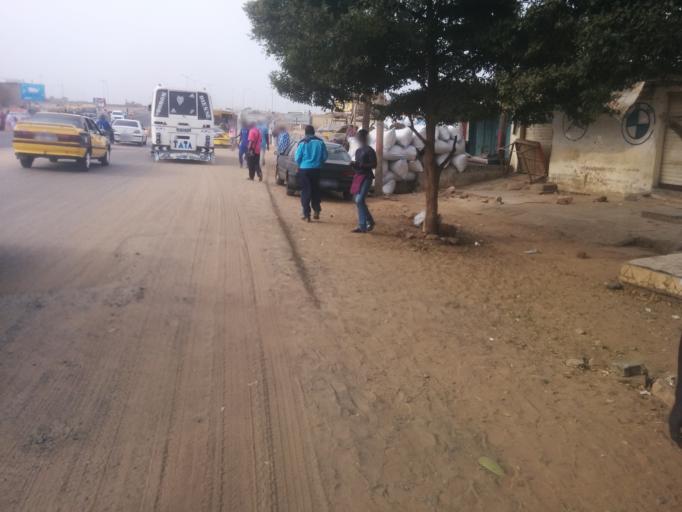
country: SN
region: Dakar
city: Grand Dakar
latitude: 14.7465
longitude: -17.4457
